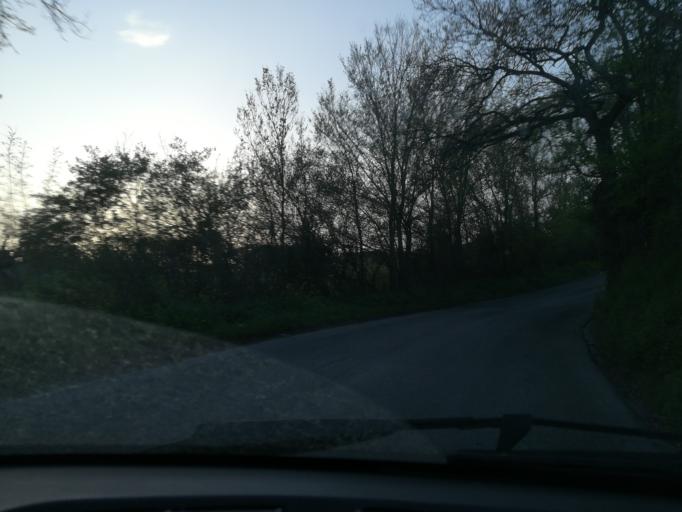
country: IT
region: The Marches
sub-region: Provincia di Macerata
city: Macerata
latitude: 43.2782
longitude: 13.4494
